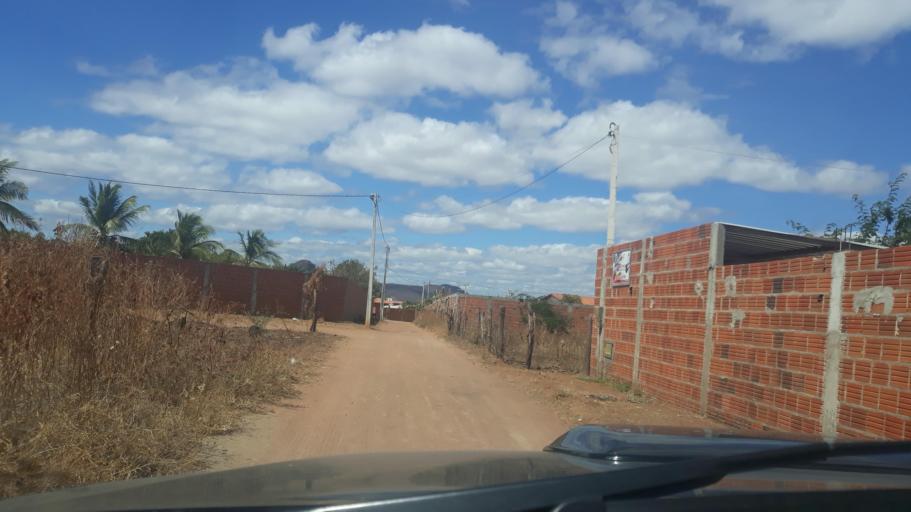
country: BR
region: Bahia
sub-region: Riacho De Santana
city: Riacho de Santana
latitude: -13.9037
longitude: -42.8515
